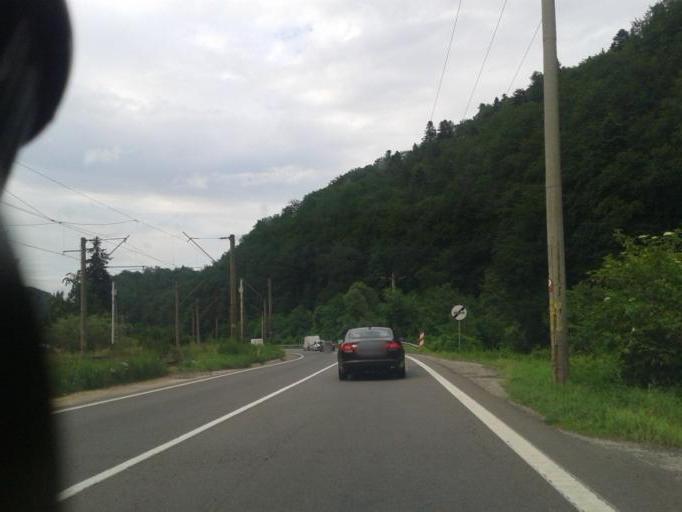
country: RO
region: Brasov
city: Brasov
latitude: 45.5774
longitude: 25.6180
